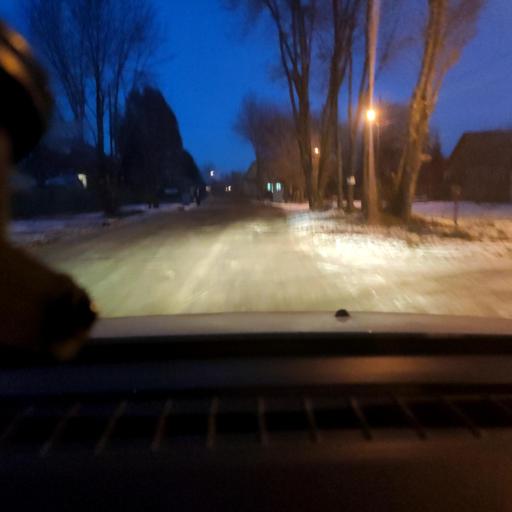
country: RU
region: Samara
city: Petra-Dubrava
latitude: 53.2559
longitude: 50.3389
